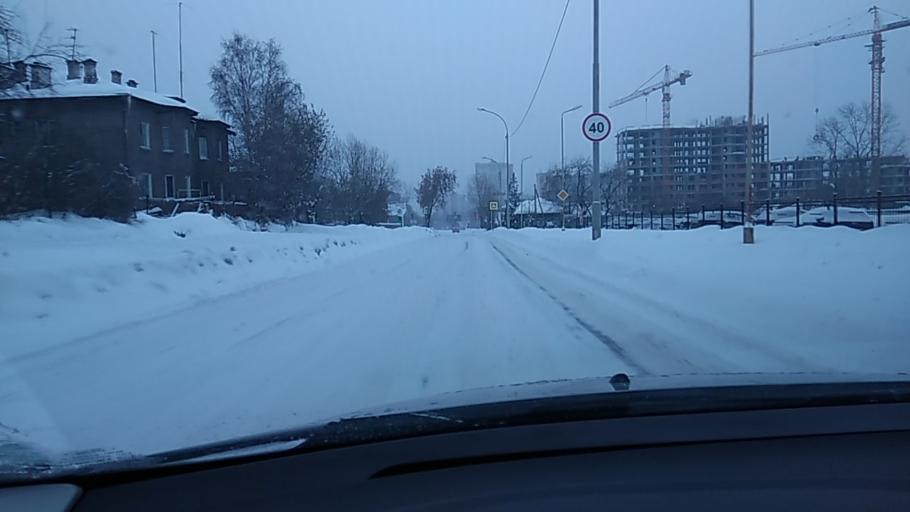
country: RU
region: Sverdlovsk
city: Sovkhoznyy
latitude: 56.8224
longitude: 60.5499
